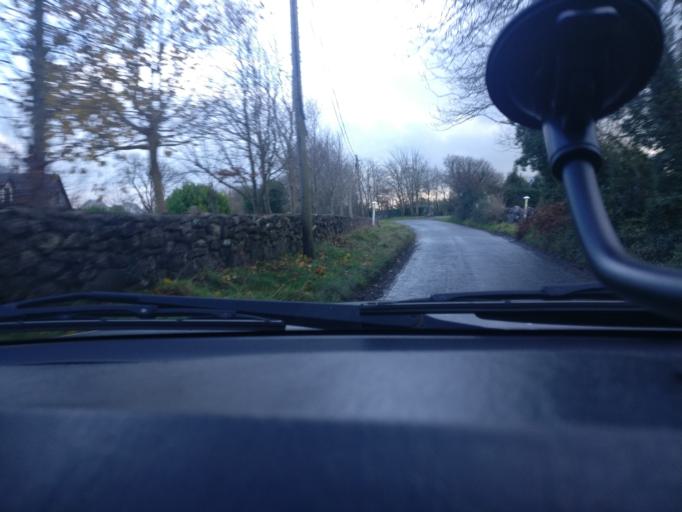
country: IE
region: Connaught
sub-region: County Galway
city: Athenry
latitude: 53.2031
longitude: -8.7145
